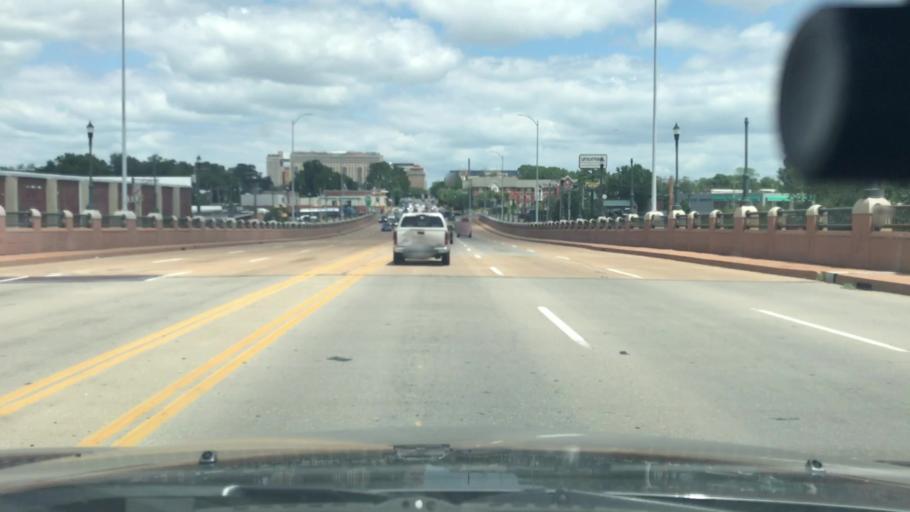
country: US
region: Missouri
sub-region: Saint Louis County
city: Richmond Heights
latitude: 38.6235
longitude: -90.2655
